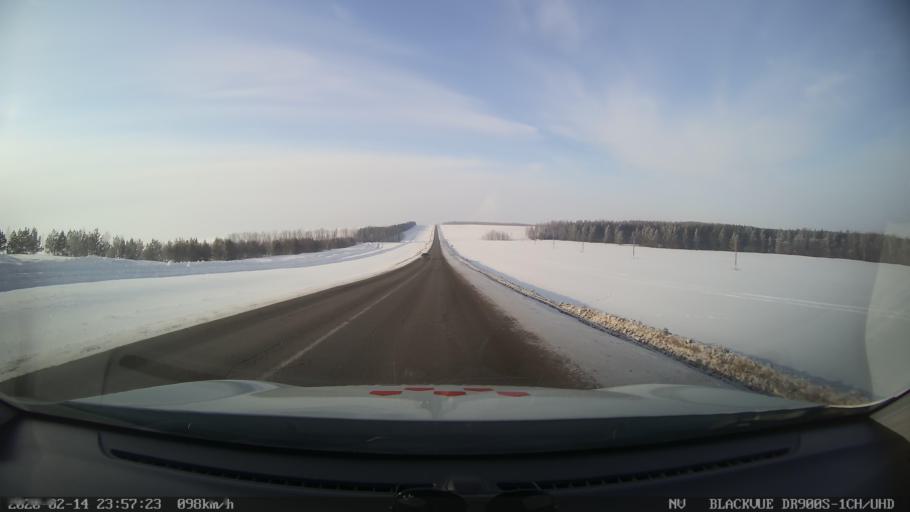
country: RU
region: Tatarstan
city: Kuybyshevskiy Zaton
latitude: 55.3336
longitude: 49.1107
